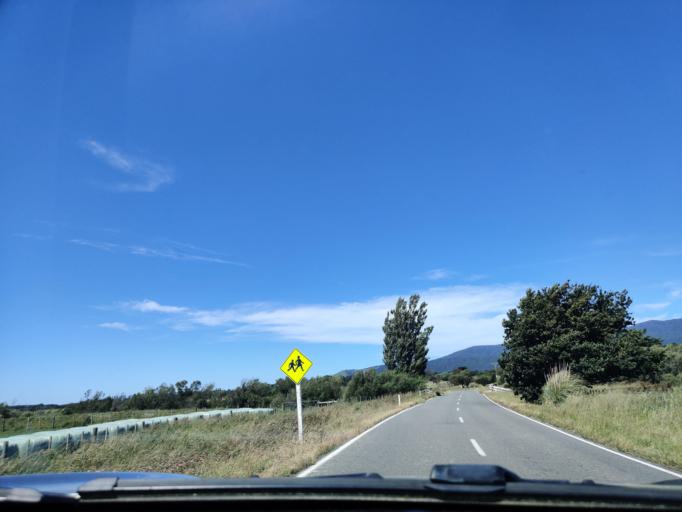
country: NZ
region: Wellington
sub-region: Upper Hutt City
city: Upper Hutt
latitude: -41.3277
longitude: 175.2185
